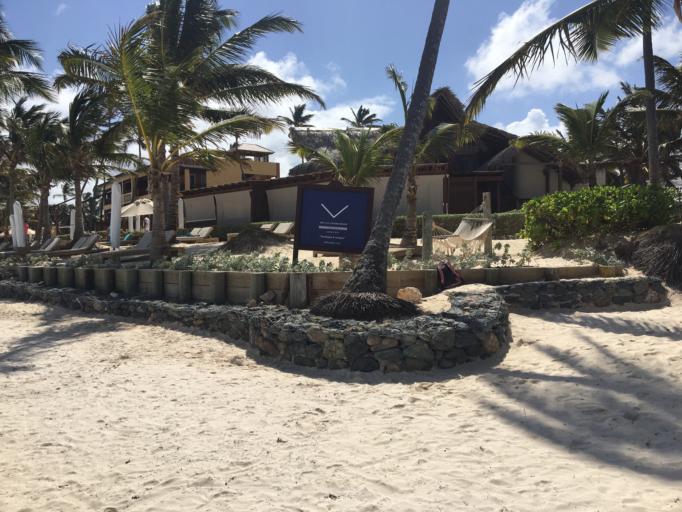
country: DO
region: San Juan
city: Punta Cana
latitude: 18.7090
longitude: -68.4417
